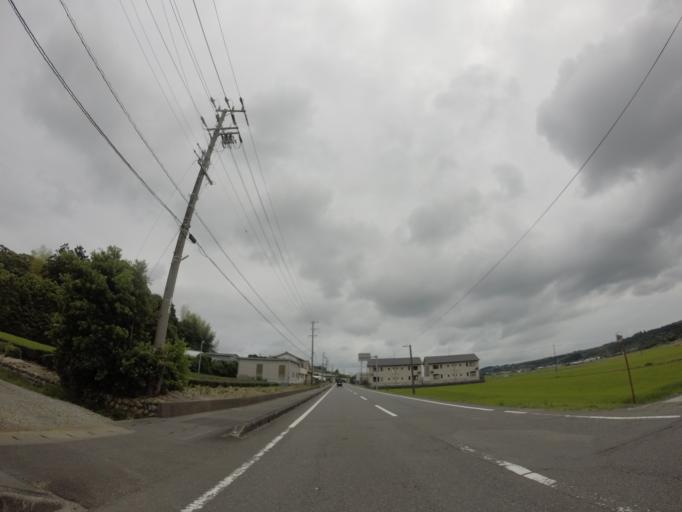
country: JP
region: Shizuoka
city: Shimada
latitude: 34.7574
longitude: 138.2044
